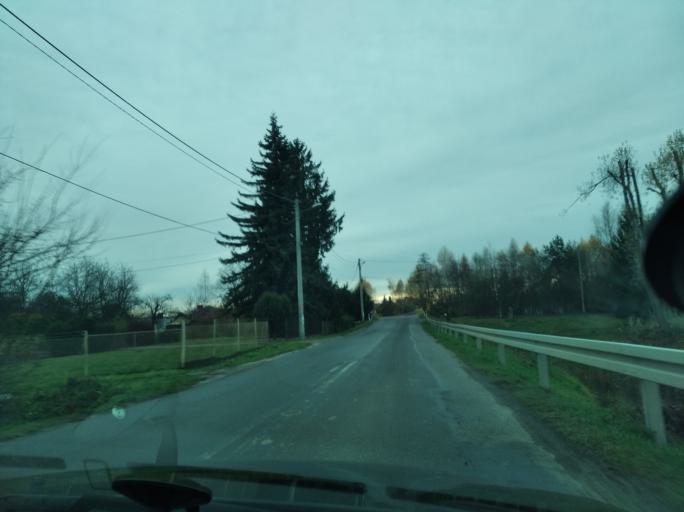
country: PL
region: Subcarpathian Voivodeship
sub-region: Powiat lancucki
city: Czarna
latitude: 50.0900
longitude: 22.1848
